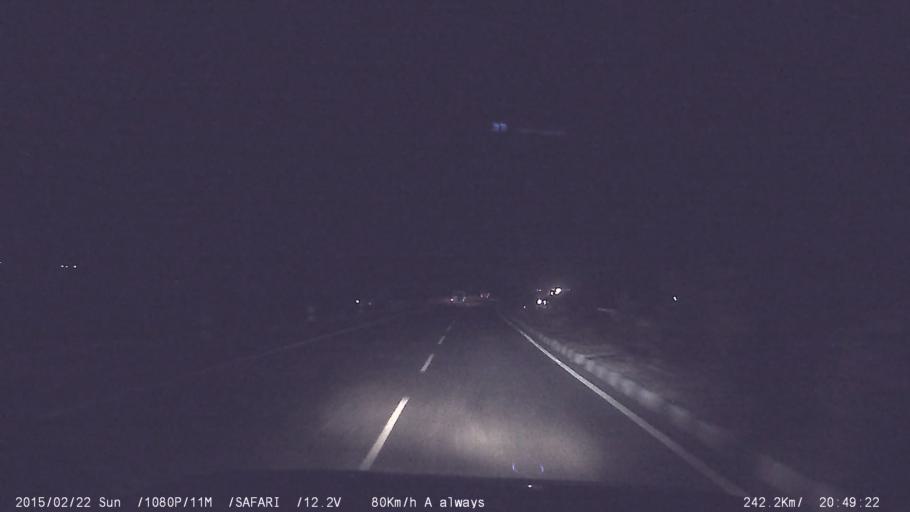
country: IN
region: Tamil Nadu
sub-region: Dindigul
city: Vedasandur
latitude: 10.5169
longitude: 77.9350
